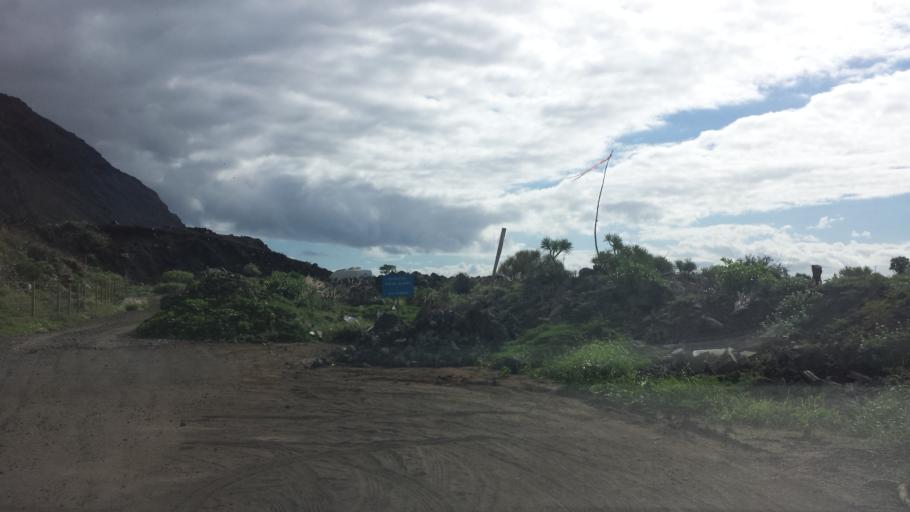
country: ES
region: Canary Islands
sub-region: Provincia de Santa Cruz de Tenerife
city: Fuencaliente de la Palma
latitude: 28.5522
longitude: -17.8860
